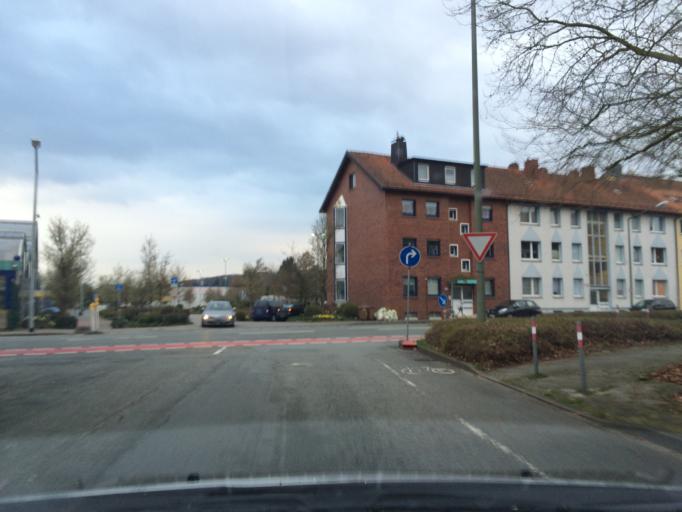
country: DE
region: Lower Saxony
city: Osnabrueck
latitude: 52.2635
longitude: 8.0638
